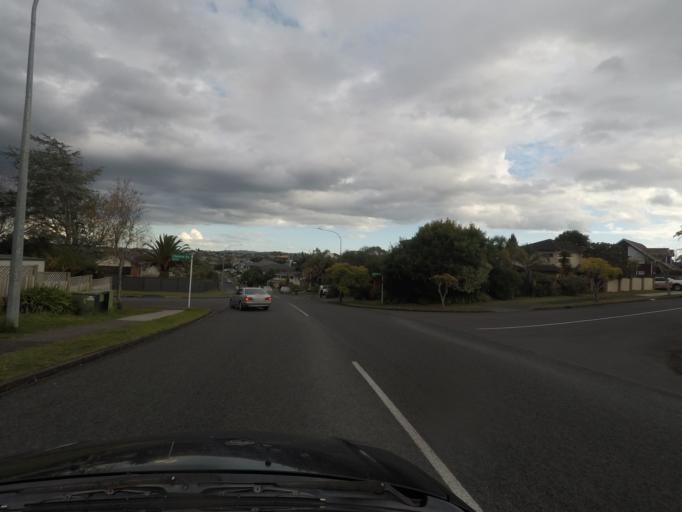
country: NZ
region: Auckland
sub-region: Auckland
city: Rosebank
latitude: -36.8058
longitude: 174.6419
